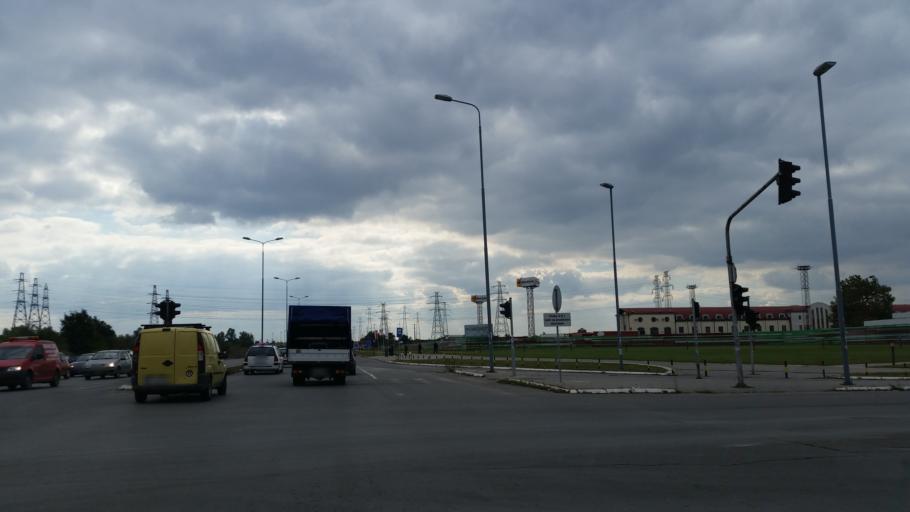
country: RS
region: Central Serbia
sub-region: Belgrade
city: Zemun
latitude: 44.8267
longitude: 20.3621
